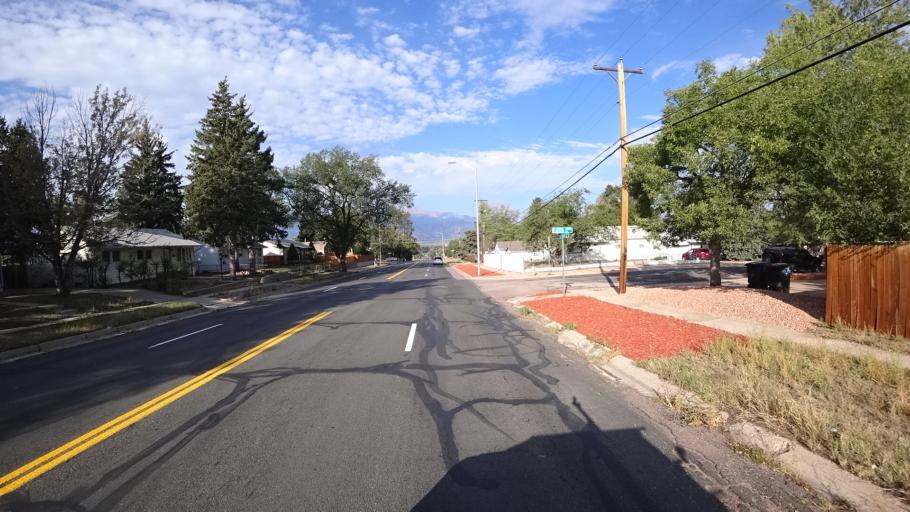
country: US
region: Colorado
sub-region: El Paso County
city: Colorado Springs
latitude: 38.8545
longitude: -104.7721
